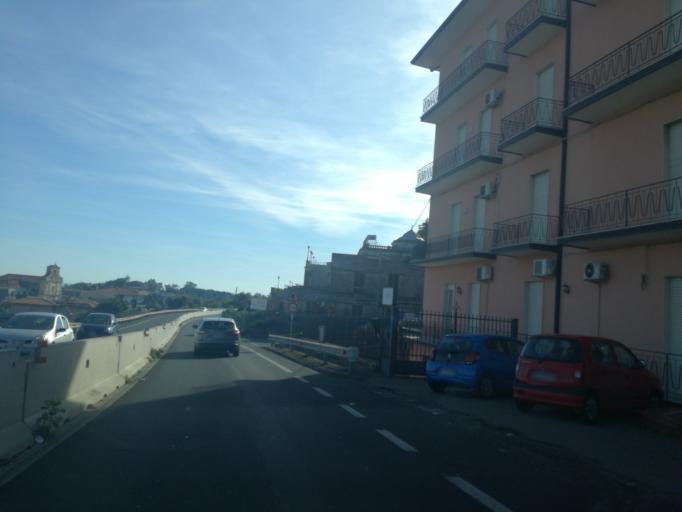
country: IT
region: Sicily
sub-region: Catania
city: Acireale
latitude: 37.6058
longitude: 15.1688
